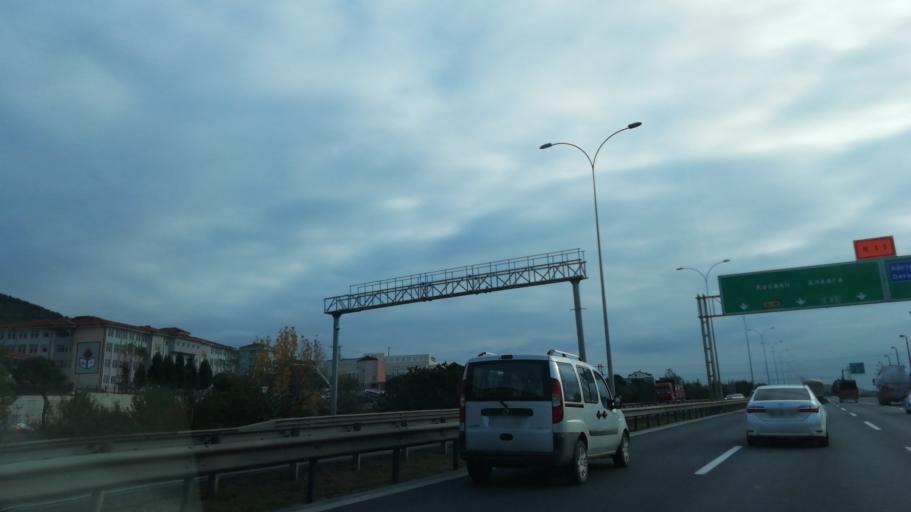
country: TR
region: Kocaeli
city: Korfez
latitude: 40.7737
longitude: 29.7643
